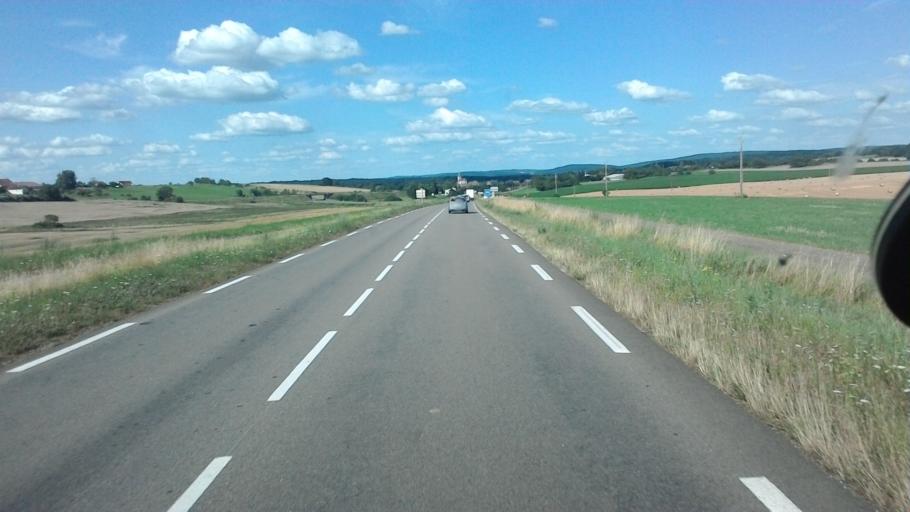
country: FR
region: Franche-Comte
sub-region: Departement de la Haute-Saone
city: Gy
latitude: 47.4758
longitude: 5.9297
